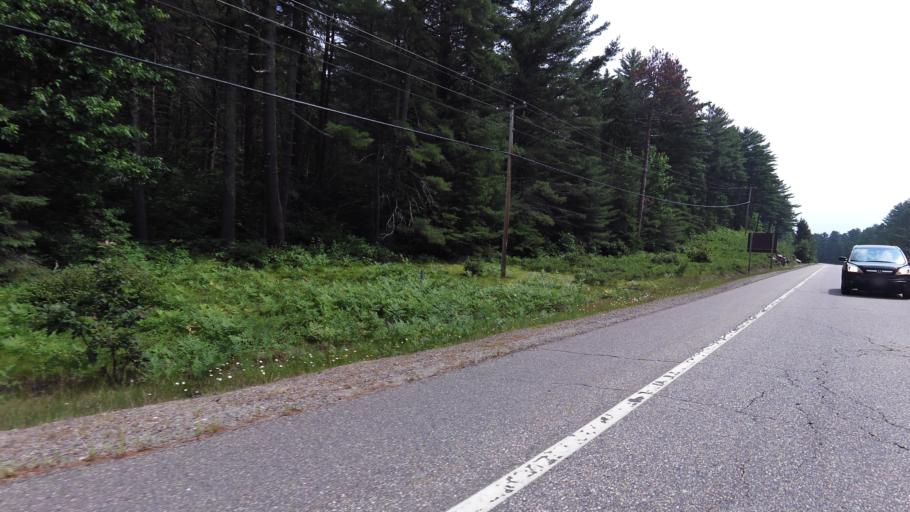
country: CA
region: Ontario
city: Huntsville
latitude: 45.5802
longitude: -78.5056
